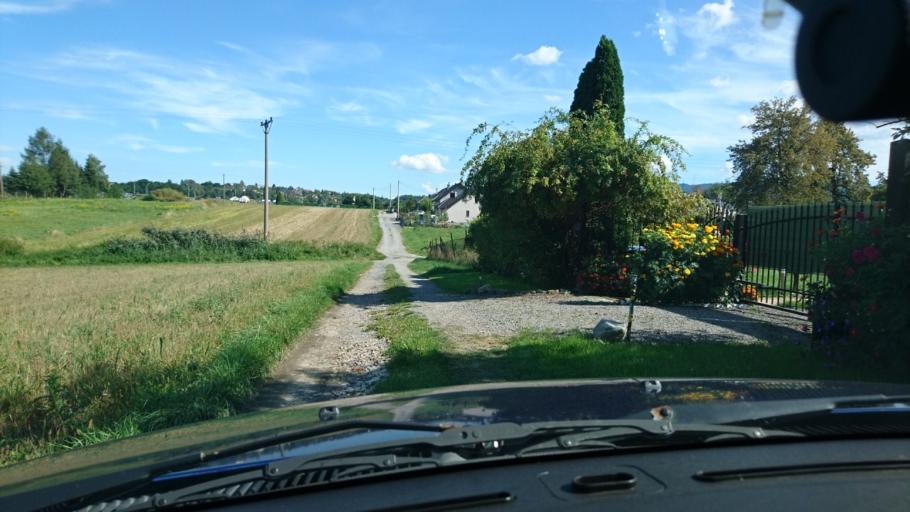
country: PL
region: Silesian Voivodeship
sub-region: Bielsko-Biala
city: Bielsko-Biala
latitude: 49.8450
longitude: 19.0613
